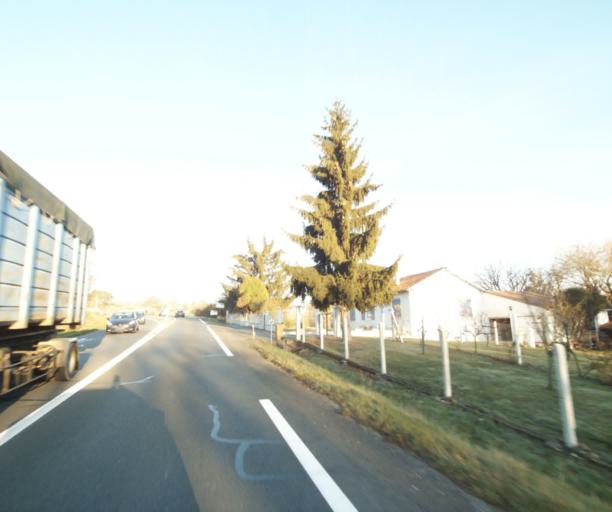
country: FR
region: Poitou-Charentes
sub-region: Departement de la Charente-Maritime
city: Chaniers
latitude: 45.7390
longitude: -0.5422
